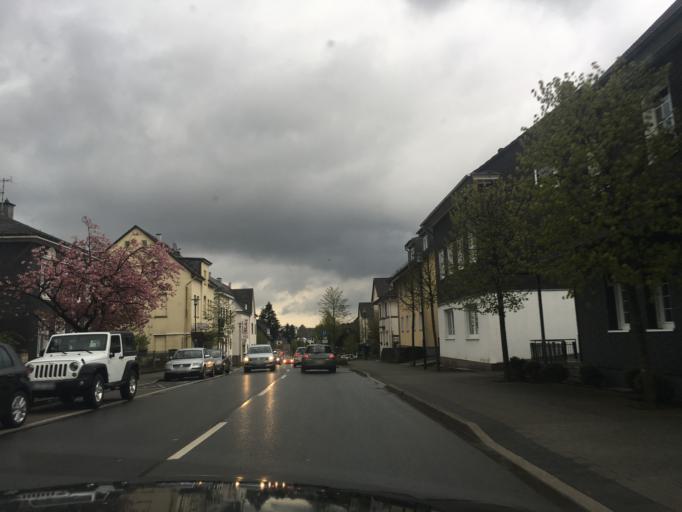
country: DE
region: North Rhine-Westphalia
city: Burscheid
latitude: 51.1045
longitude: 7.1589
